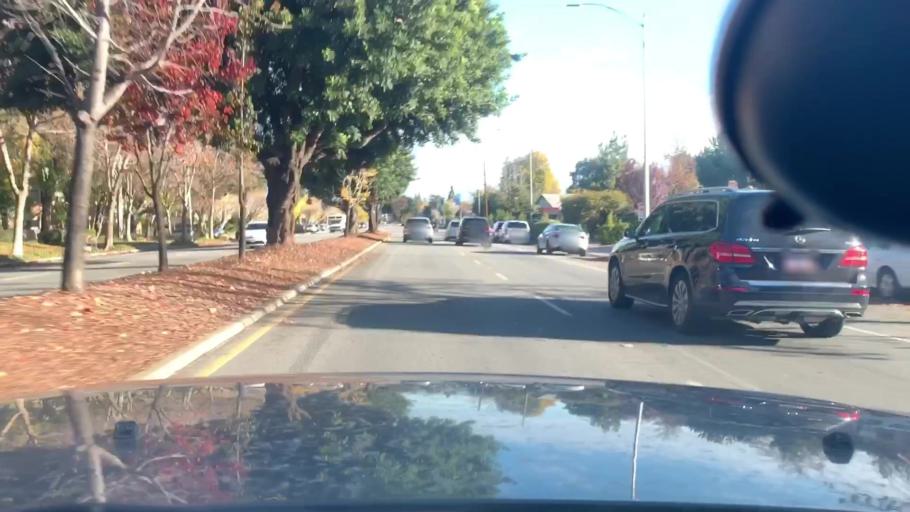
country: US
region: California
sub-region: Santa Clara County
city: Campbell
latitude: 37.2960
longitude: -121.9870
